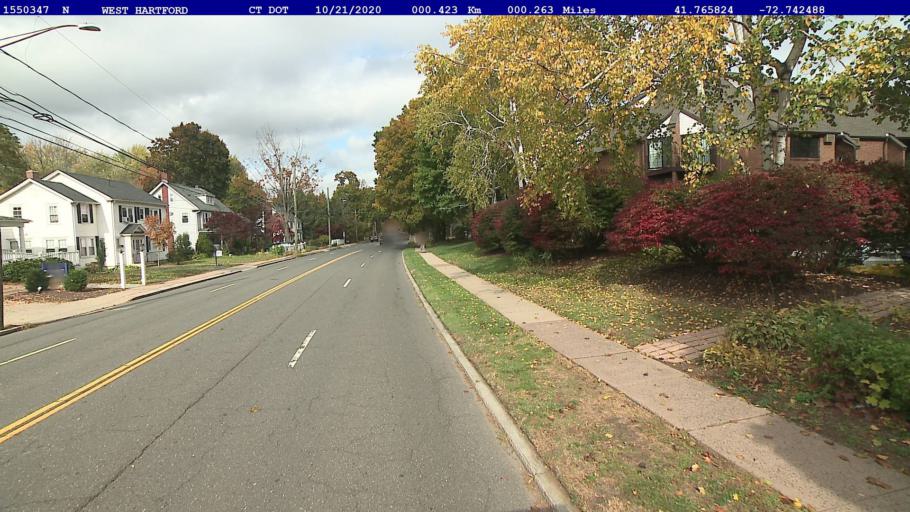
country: US
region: Connecticut
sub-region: Hartford County
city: West Hartford
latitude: 41.7658
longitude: -72.7425
